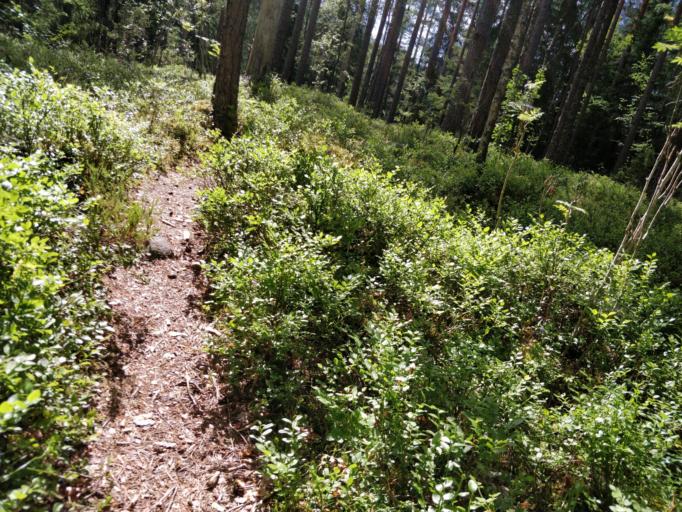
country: FI
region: Uusimaa
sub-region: Helsinki
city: Vihti
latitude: 60.3136
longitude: 24.4699
